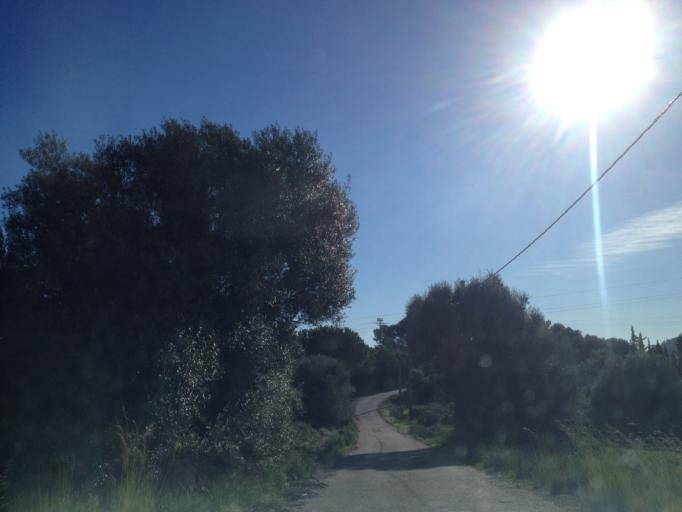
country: ES
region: Balearic Islands
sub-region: Illes Balears
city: Sineu
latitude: 39.6539
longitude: 3.0350
